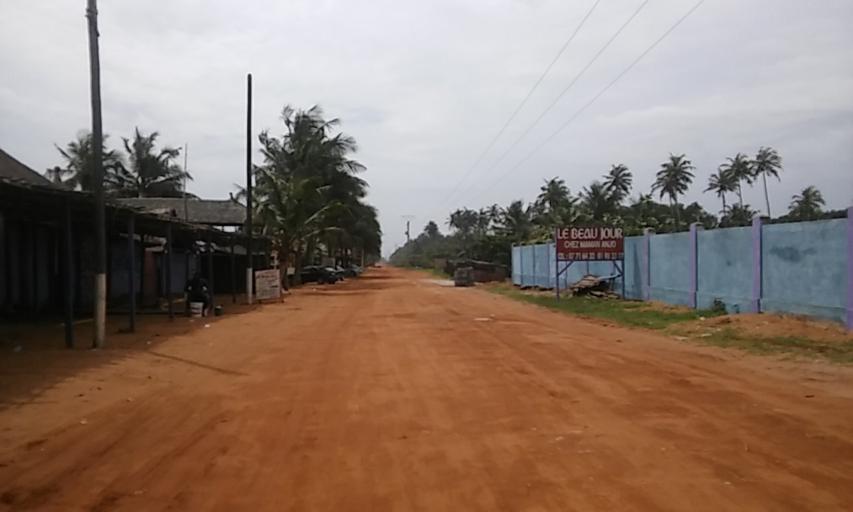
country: CI
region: Sud-Comoe
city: Grand-Bassam
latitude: 5.1976
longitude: -3.7537
